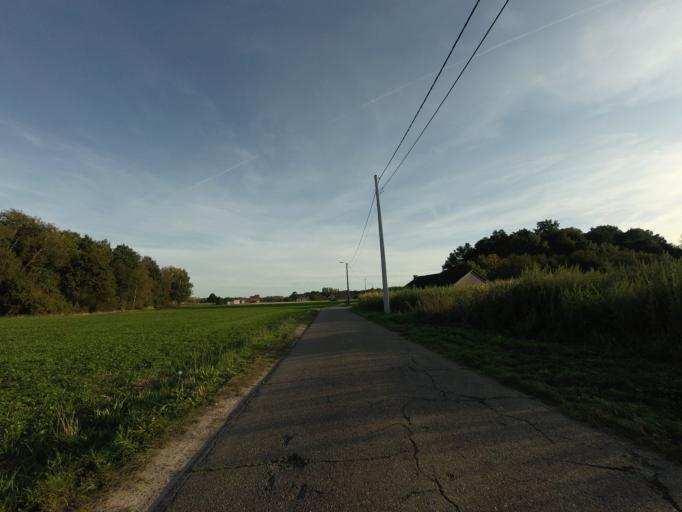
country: BE
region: Flanders
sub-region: Provincie Vlaams-Brabant
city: Kampenhout
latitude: 50.9392
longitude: 4.5894
